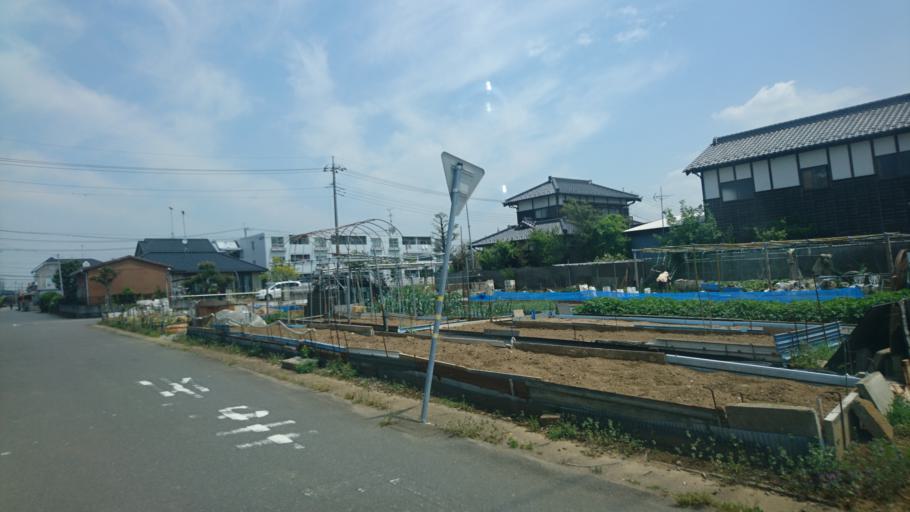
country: JP
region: Ibaraki
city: Mitsukaido
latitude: 36.0106
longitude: 139.9882
